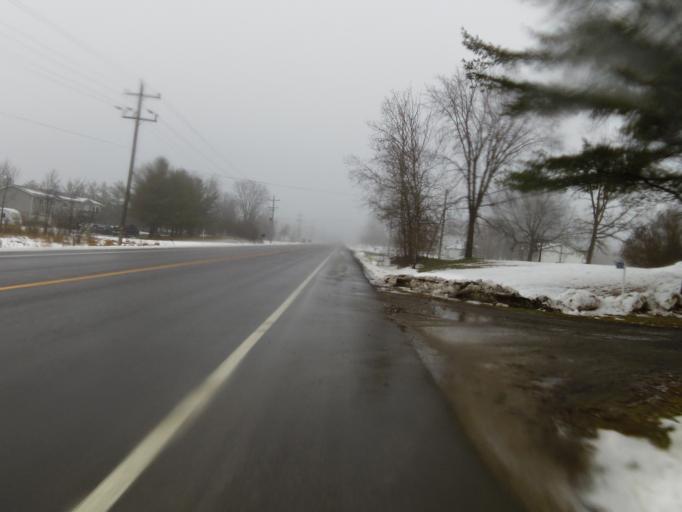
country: CA
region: Ontario
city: Perth
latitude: 44.8849
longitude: -76.3049
